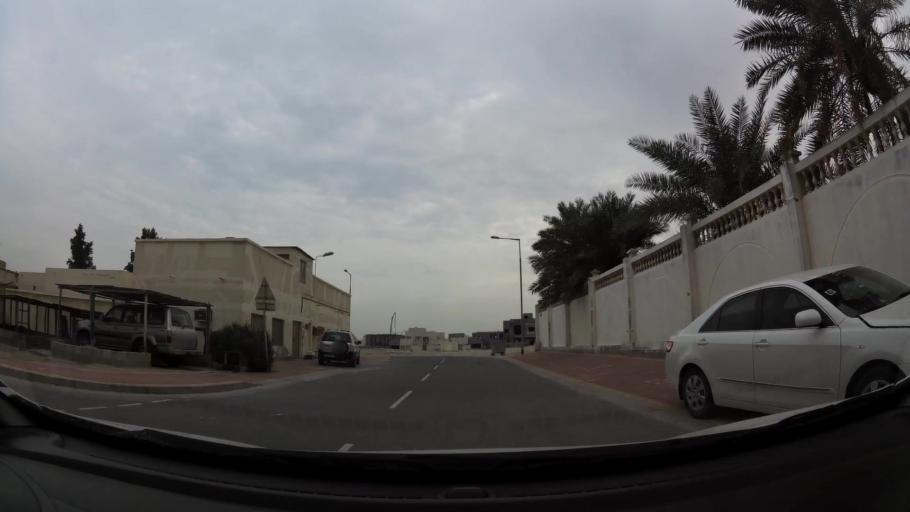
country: BH
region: Northern
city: Ar Rifa'
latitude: 26.0549
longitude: 50.6172
